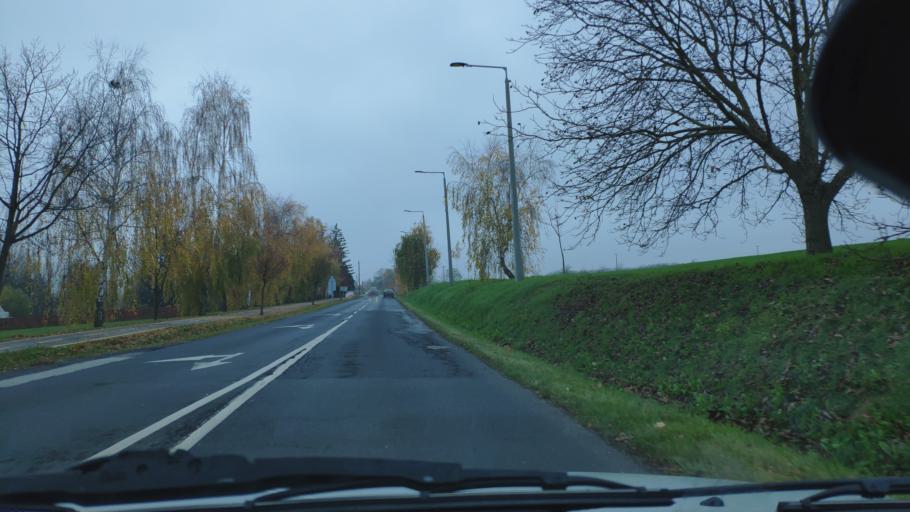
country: HU
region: Zala
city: Zalakomar
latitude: 46.5415
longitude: 17.1262
